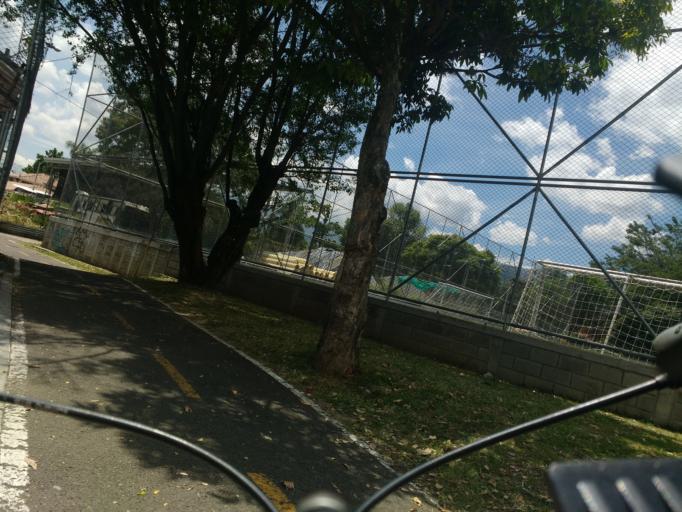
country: CO
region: Antioquia
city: Itagui
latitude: 6.2140
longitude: -75.5873
